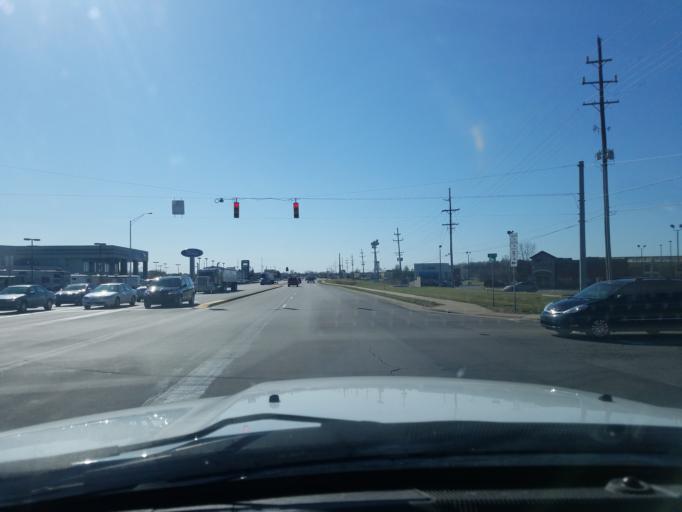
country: US
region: Indiana
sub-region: Shelby County
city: Shelbyville
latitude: 39.5258
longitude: -85.7376
